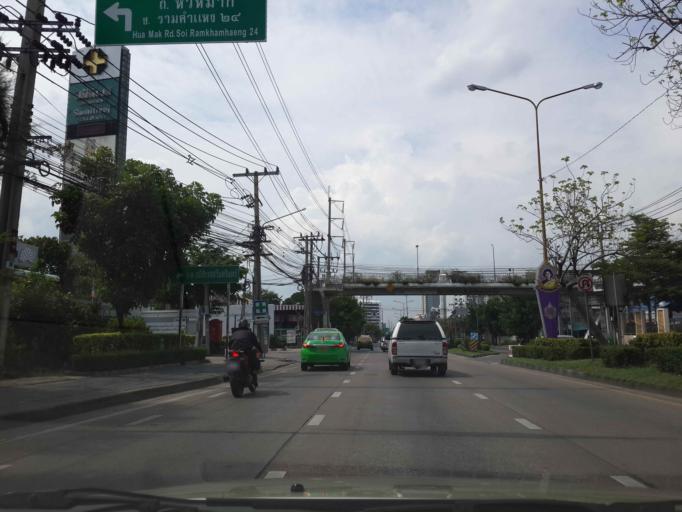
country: TH
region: Bangkok
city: Suan Luang
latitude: 13.7453
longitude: 100.6434
